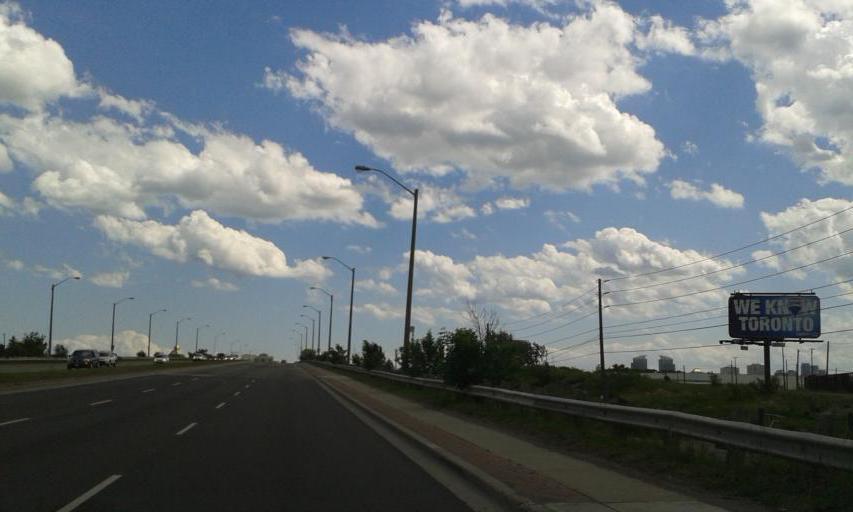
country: CA
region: Ontario
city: Scarborough
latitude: 43.8058
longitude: -79.2438
